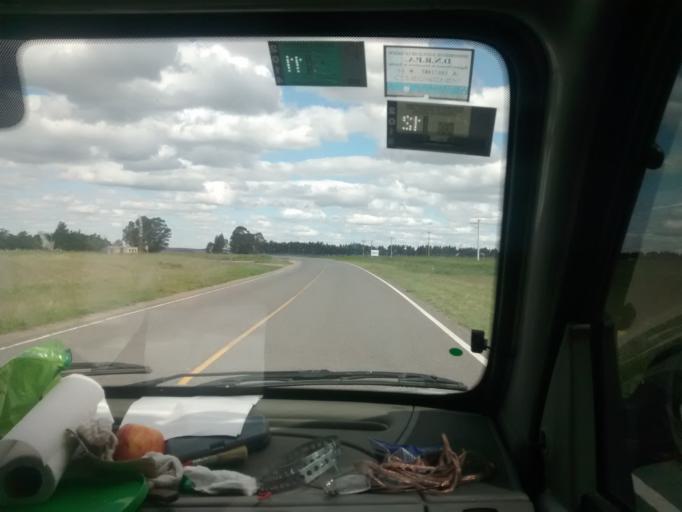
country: AR
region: Buenos Aires
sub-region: Partido de Balcarce
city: Balcarce
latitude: -37.6377
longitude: -58.4919
